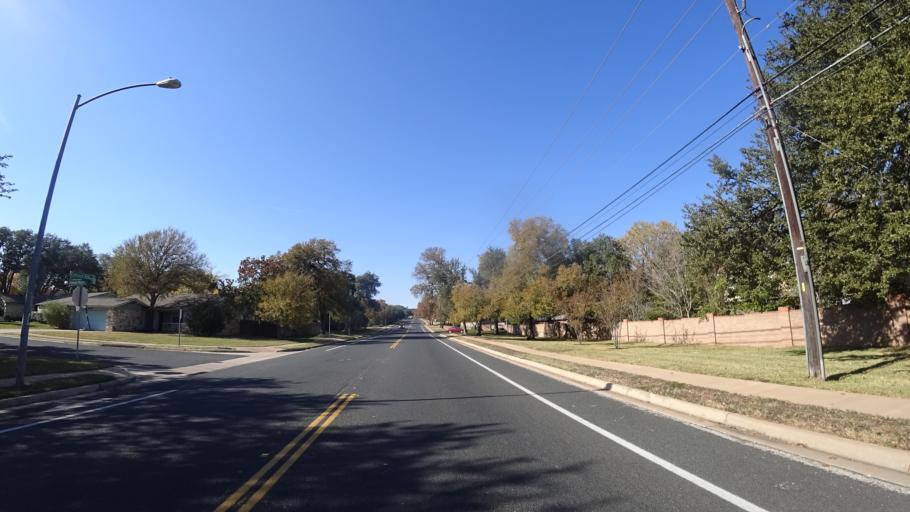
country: US
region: Texas
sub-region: Travis County
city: Shady Hollow
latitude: 30.2232
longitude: -97.8633
